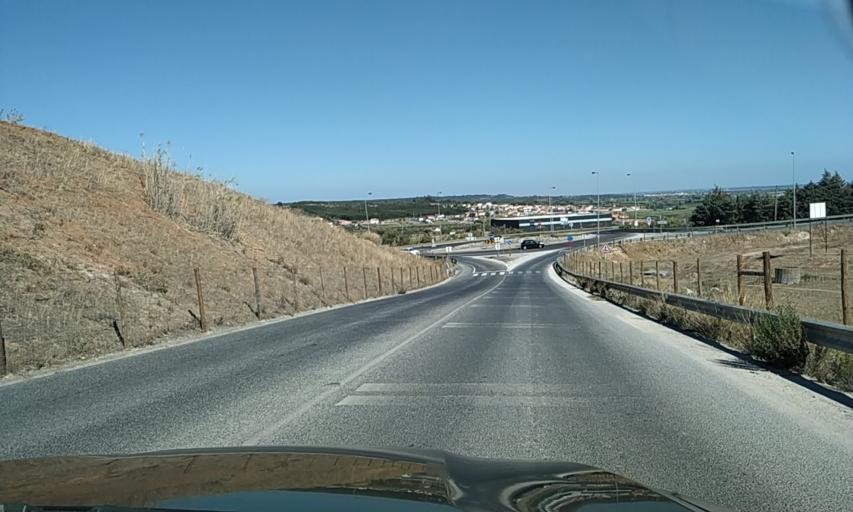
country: PT
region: Lisbon
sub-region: Alenquer
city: Alenquer
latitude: 39.0660
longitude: -9.0016
